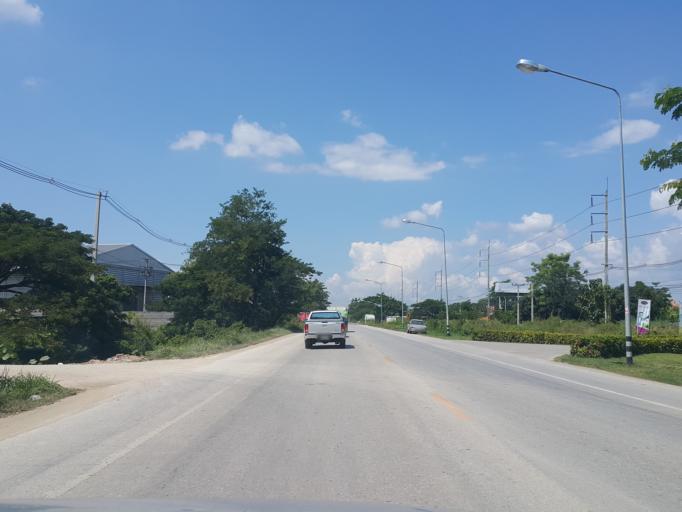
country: TH
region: Chiang Mai
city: San Sai
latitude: 18.8079
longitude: 99.0588
